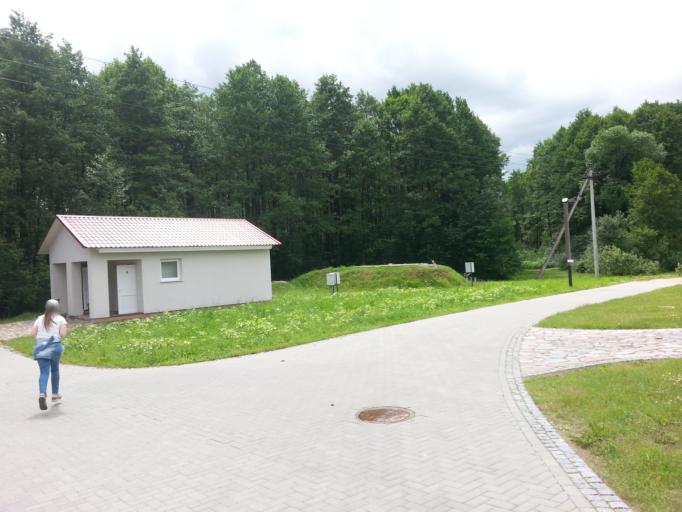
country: BY
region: Minsk
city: Narach
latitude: 54.8614
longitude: 26.7123
